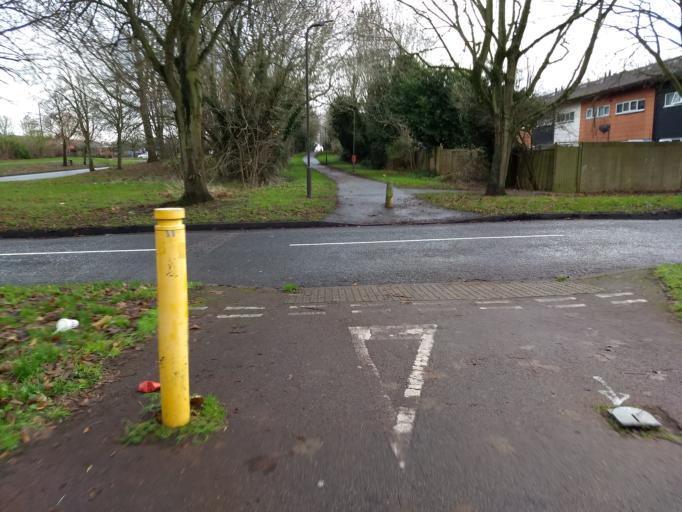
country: GB
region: England
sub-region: Buckinghamshire
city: Newton Longville
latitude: 51.9968
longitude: -0.7699
